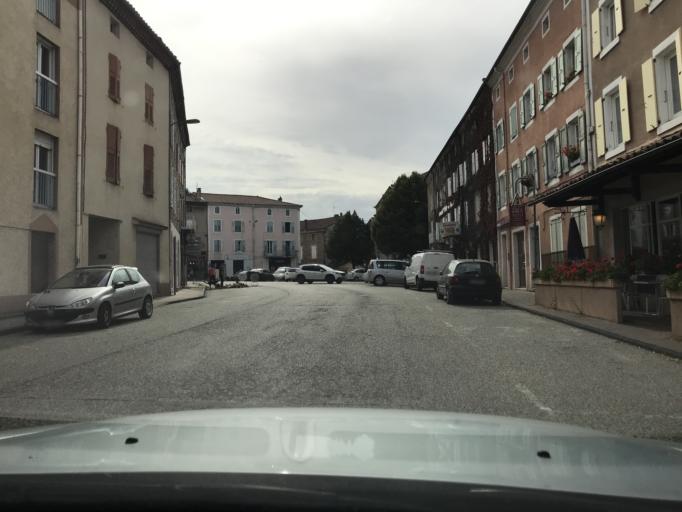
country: FR
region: Rhone-Alpes
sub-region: Departement de l'Ardeche
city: Lamastre
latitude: 44.9866
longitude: 4.5828
